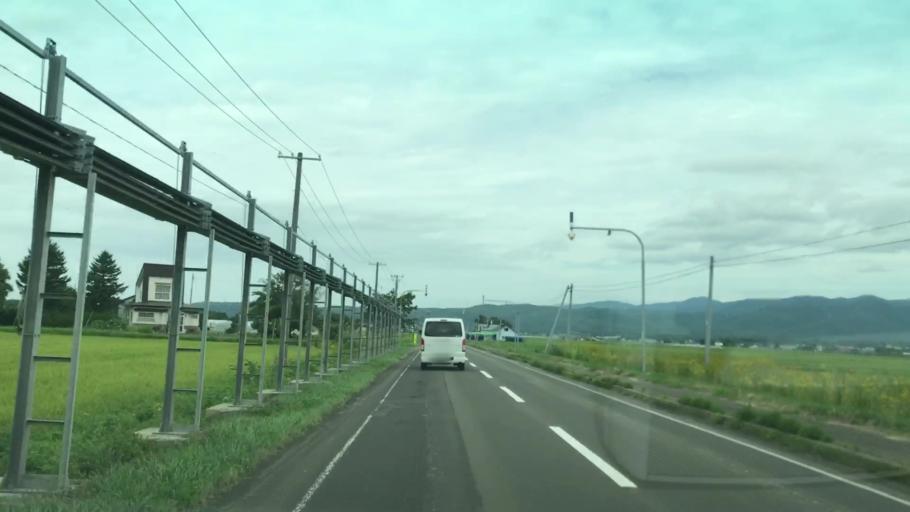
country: JP
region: Hokkaido
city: Iwanai
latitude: 43.0054
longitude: 140.5827
